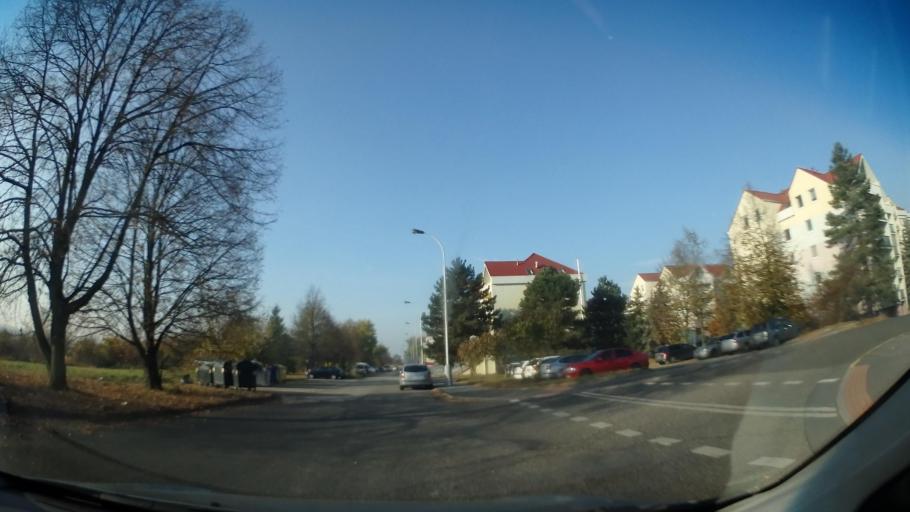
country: CZ
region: Central Bohemia
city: Sestajovice
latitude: 50.0700
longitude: 14.6798
